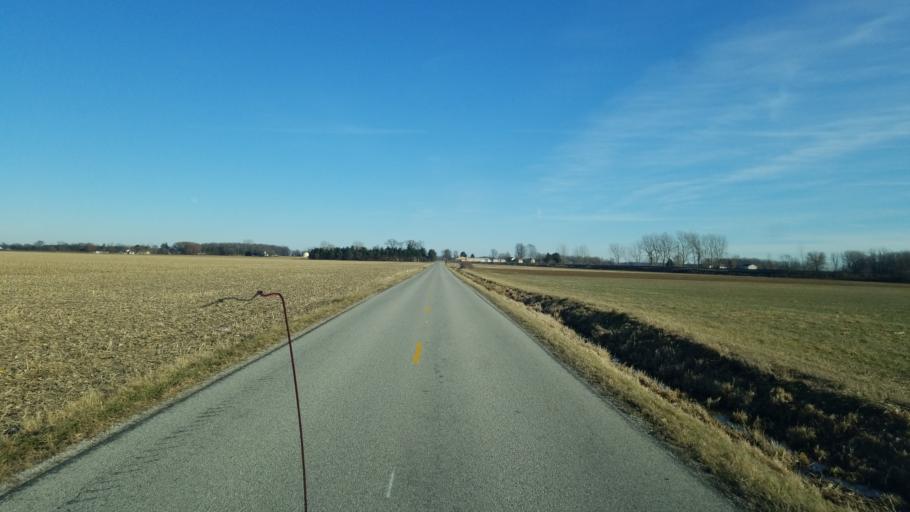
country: US
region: Ohio
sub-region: Sandusky County
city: Green Springs
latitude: 41.2562
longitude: -83.0239
